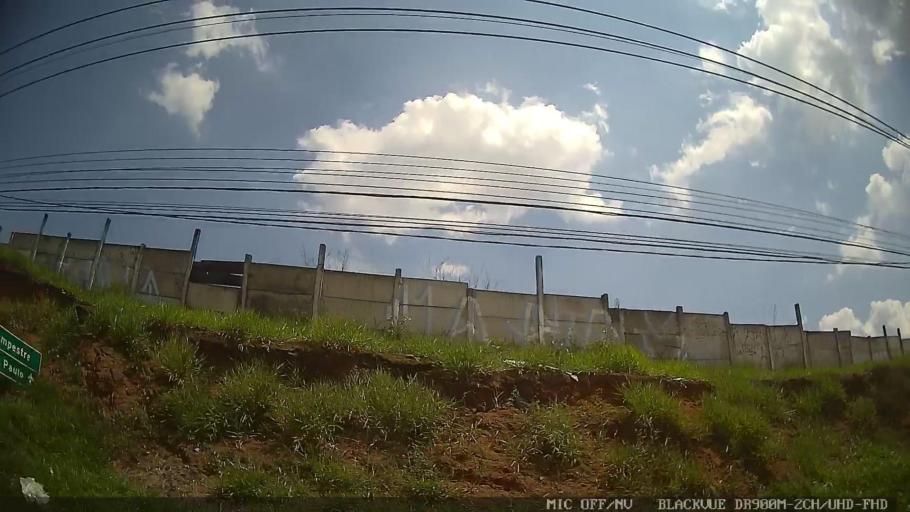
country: BR
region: Sao Paulo
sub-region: Itapecerica Da Serra
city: Itapecerica da Serra
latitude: -23.6901
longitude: -46.8163
